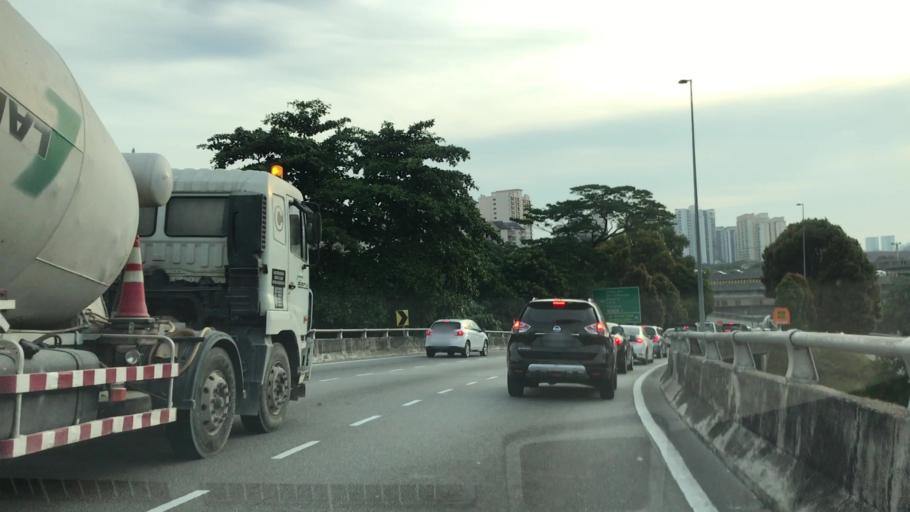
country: MY
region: Kuala Lumpur
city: Kuala Lumpur
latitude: 3.0879
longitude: 101.6967
